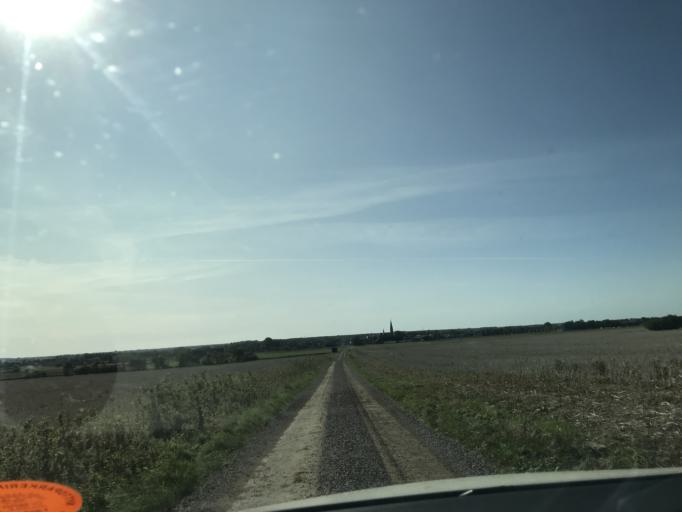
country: SE
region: Skane
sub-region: Landskrona
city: Asmundtorp
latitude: 55.9011
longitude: 12.9491
